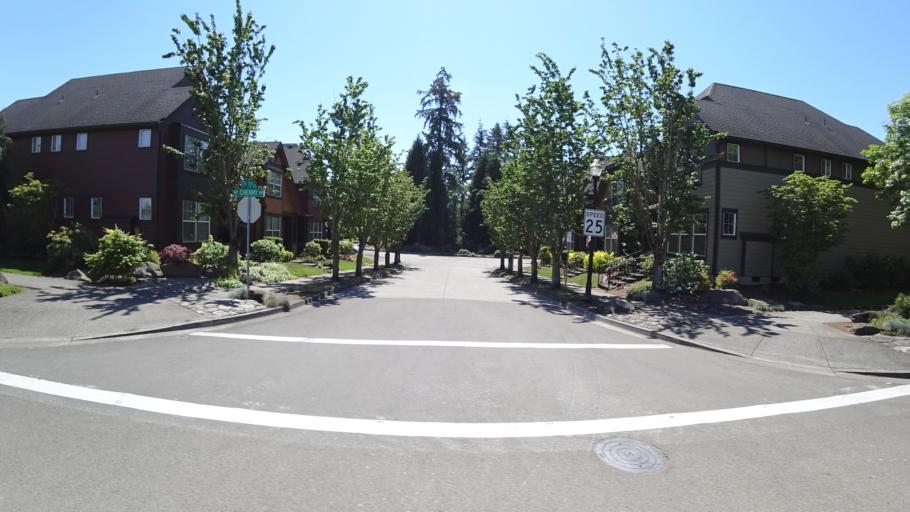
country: US
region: Oregon
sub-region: Washington County
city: Rockcreek
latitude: 45.5311
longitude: -122.9048
